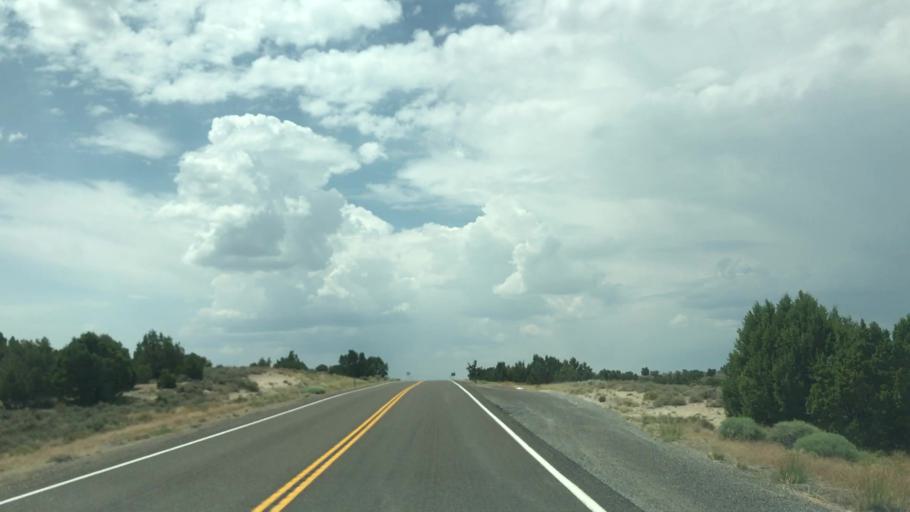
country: US
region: Nevada
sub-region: Eureka County
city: Eureka
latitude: 39.4115
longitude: -115.6944
